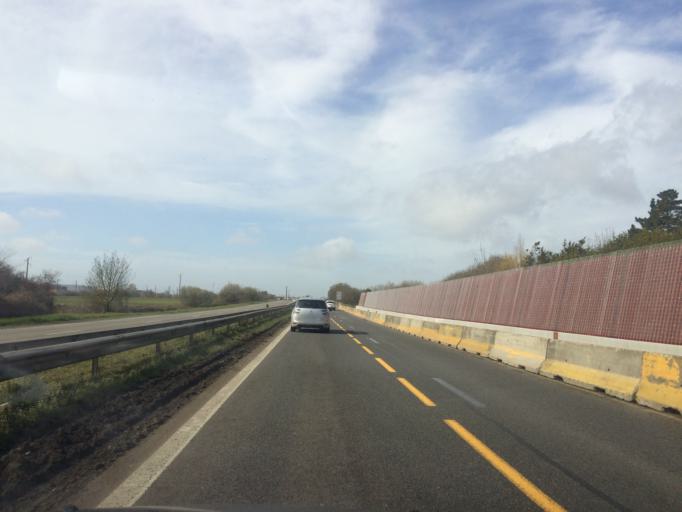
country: FR
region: Pays de la Loire
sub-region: Departement de la Loire-Atlantique
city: Montoir-de-Bretagne
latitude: 47.3257
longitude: -2.1447
